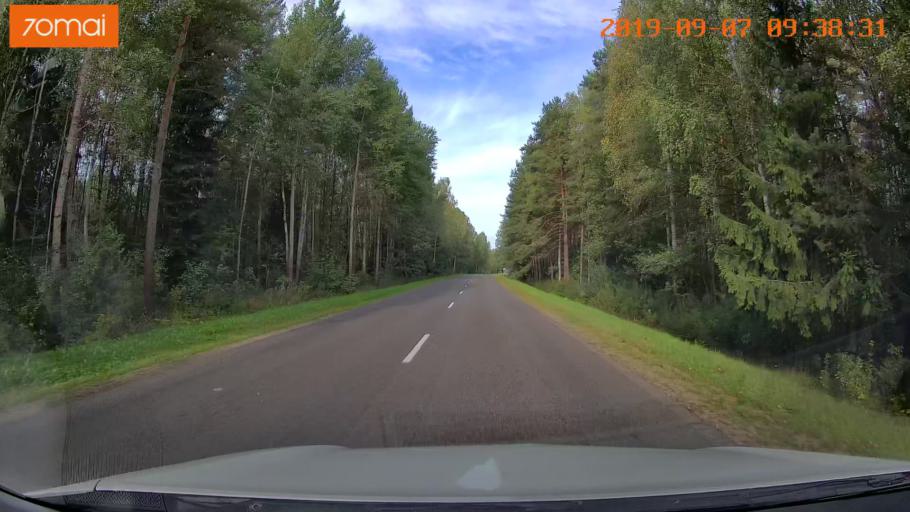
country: BY
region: Grodnenskaya
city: Iwye
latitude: 53.9244
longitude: 25.8193
